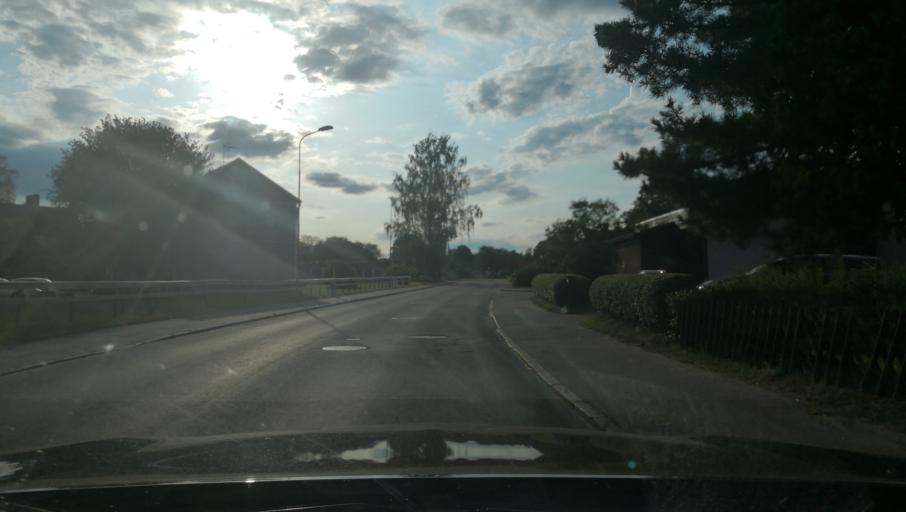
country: SE
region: Dalarna
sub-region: Ludvika Kommun
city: Ludvika
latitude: 60.1260
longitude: 15.1849
